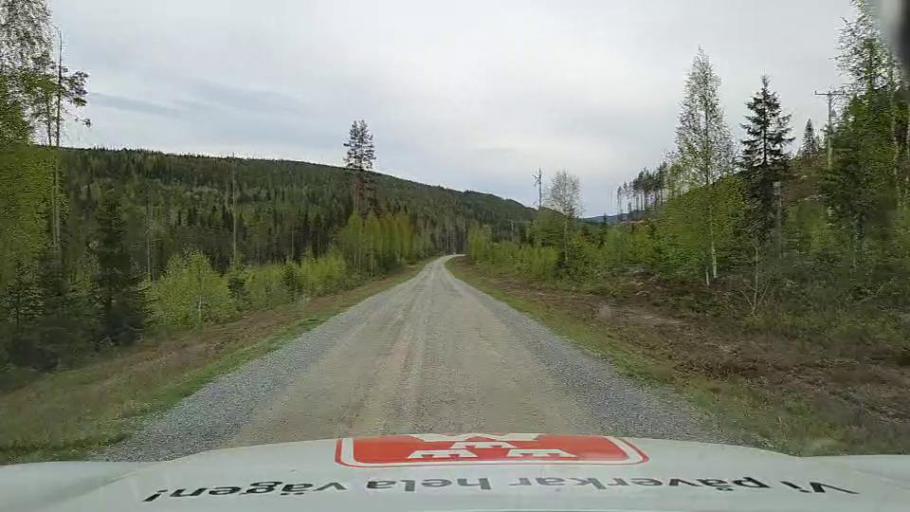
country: SE
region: Jaemtland
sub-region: Bergs Kommun
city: Hoverberg
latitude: 62.5303
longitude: 14.7090
